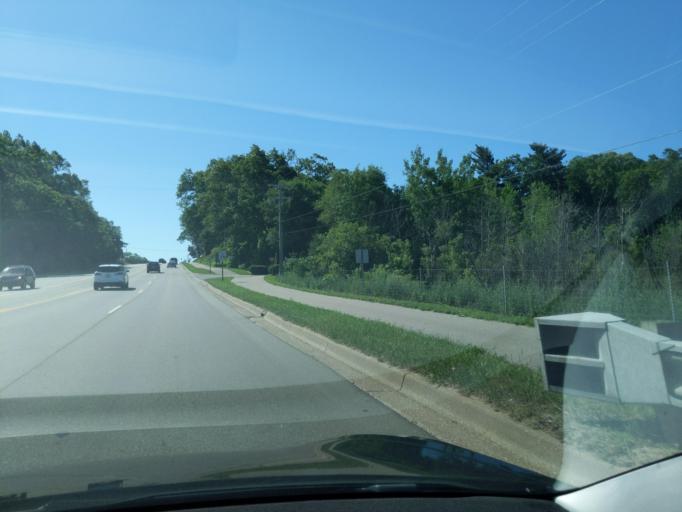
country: US
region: Michigan
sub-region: Muskegon County
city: North Muskegon
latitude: 43.2708
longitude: -86.2561
